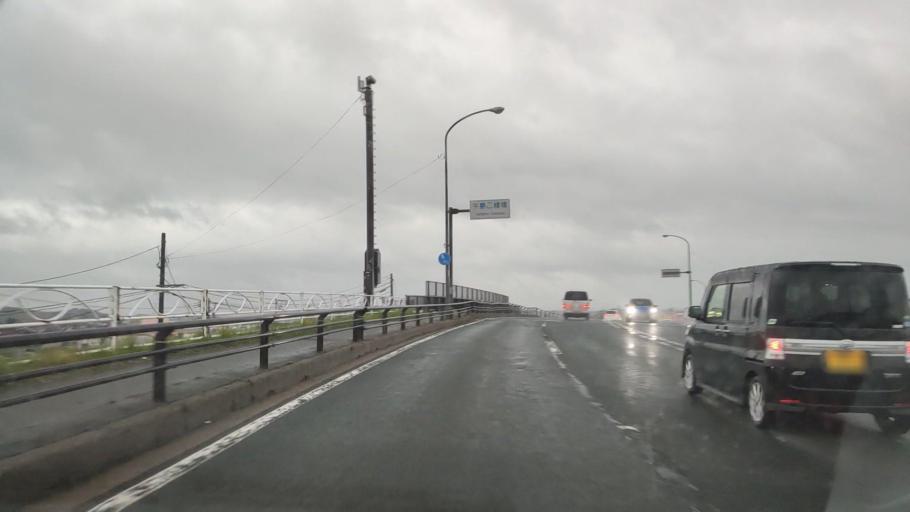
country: JP
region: Akita
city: Akita
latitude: 39.6976
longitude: 140.1180
